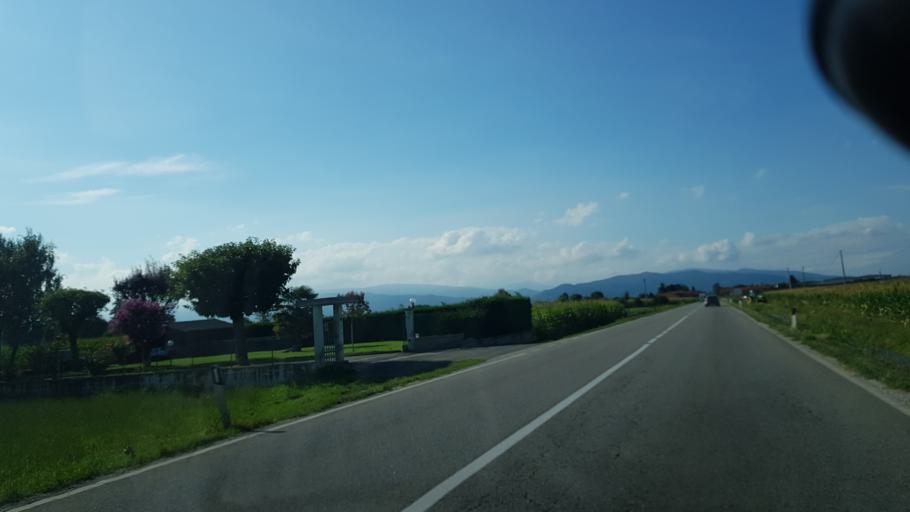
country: IT
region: Piedmont
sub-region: Provincia di Cuneo
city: Roata Rossi
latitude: 44.4329
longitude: 7.5374
